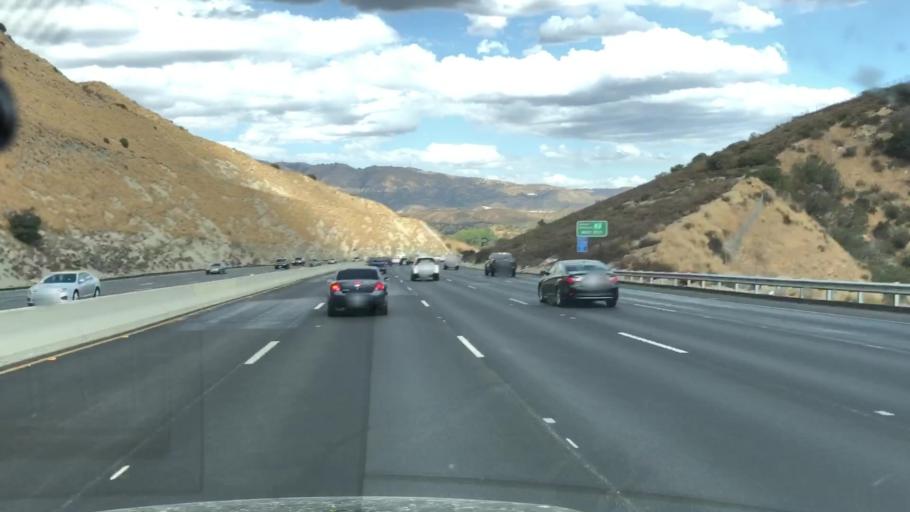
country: US
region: California
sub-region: Los Angeles County
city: Chatsworth
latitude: 34.2722
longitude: -118.6304
